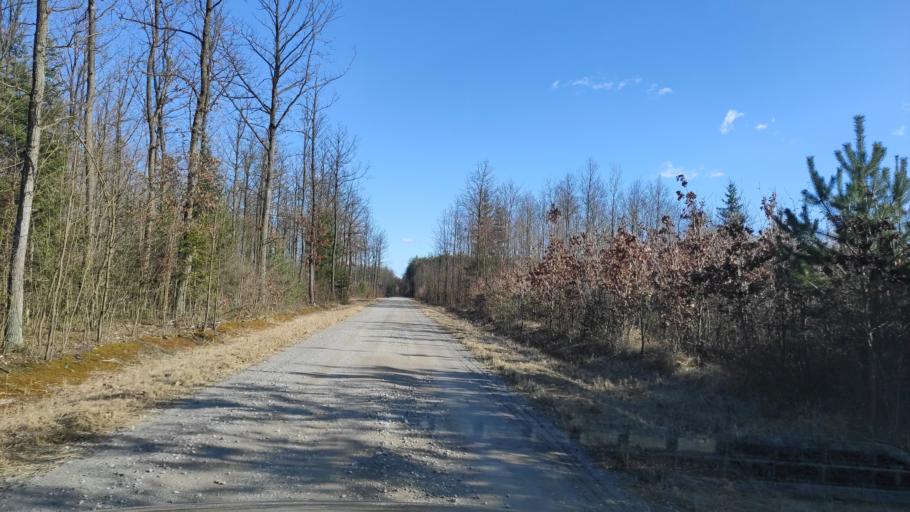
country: PL
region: Masovian Voivodeship
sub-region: Powiat radomski
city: Jedlnia-Letnisko
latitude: 51.4518
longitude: 21.2850
